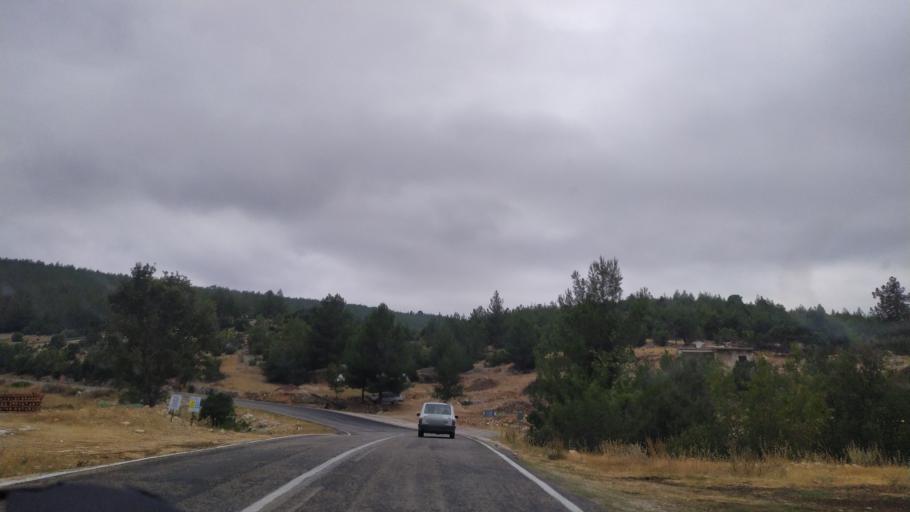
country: TR
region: Mersin
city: Silifke
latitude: 36.5410
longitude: 33.9360
